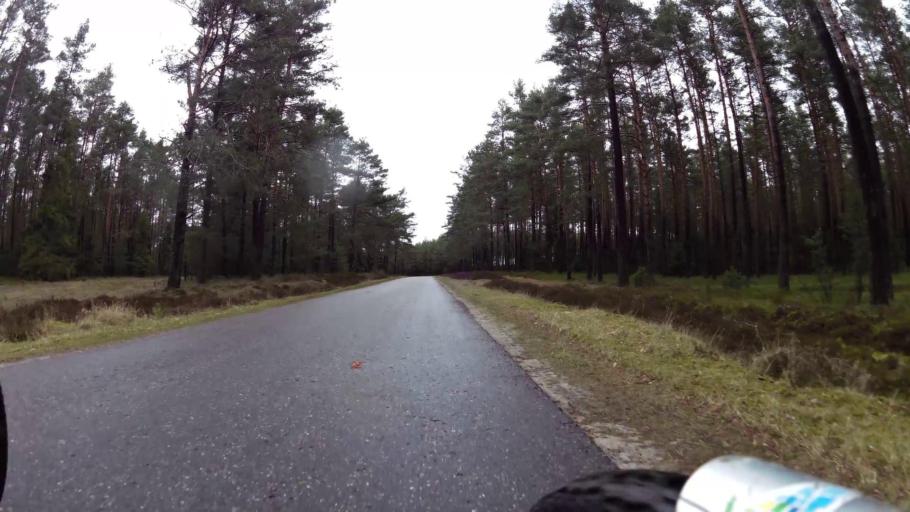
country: PL
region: Pomeranian Voivodeship
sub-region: Powiat bytowski
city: Borzytuchom
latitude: 54.2623
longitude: 17.3666
